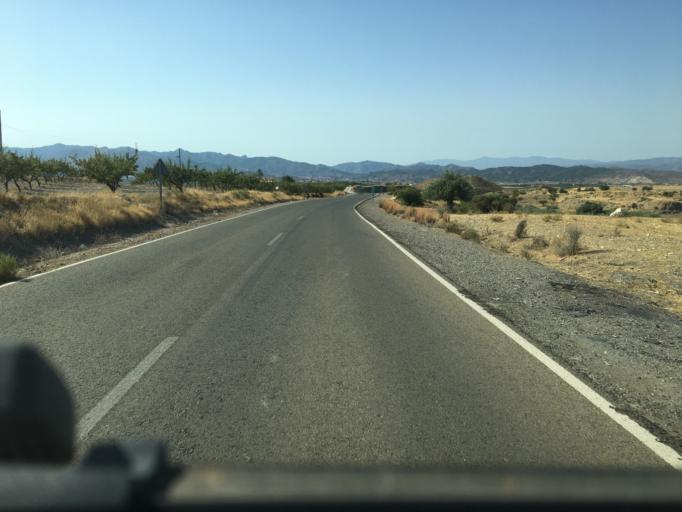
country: ES
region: Andalusia
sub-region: Provincia de Almeria
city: Huercal-Overa
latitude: 37.4372
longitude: -1.9755
